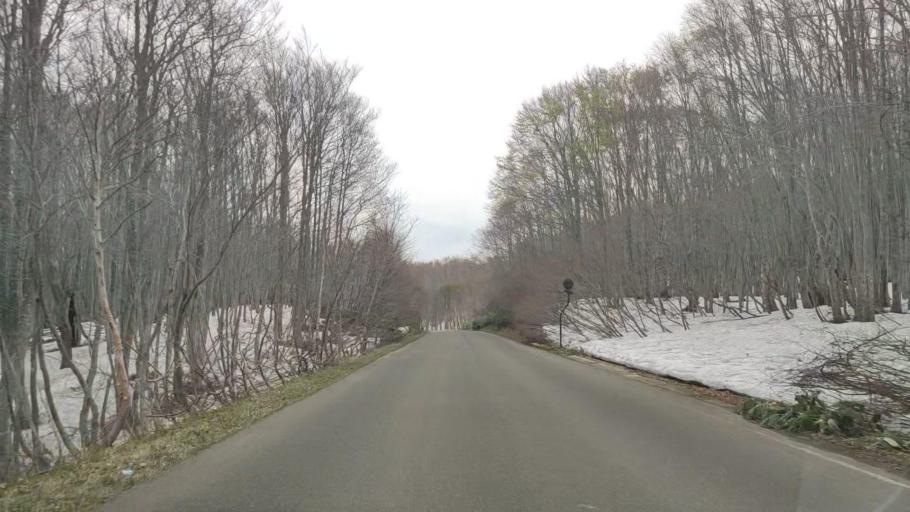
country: JP
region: Aomori
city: Aomori Shi
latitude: 40.6891
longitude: 140.9174
